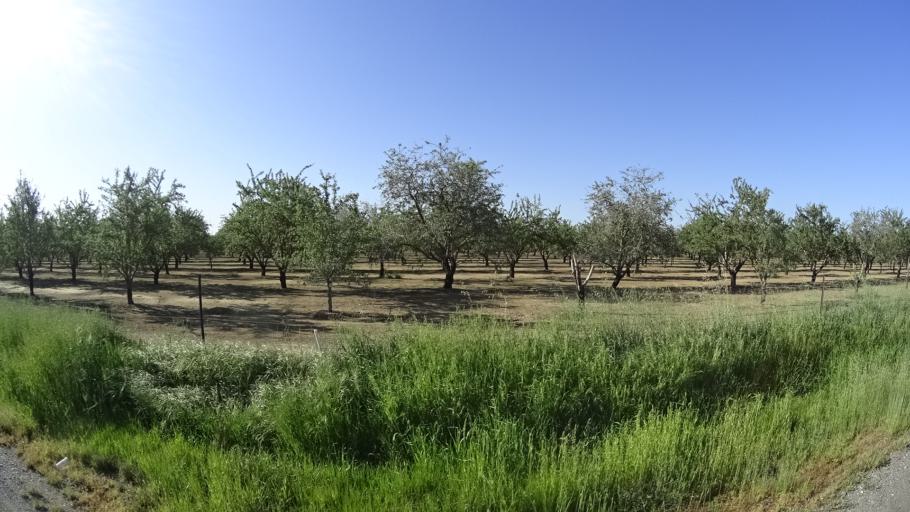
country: US
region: California
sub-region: Glenn County
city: Hamilton City
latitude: 39.6959
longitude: -122.1000
